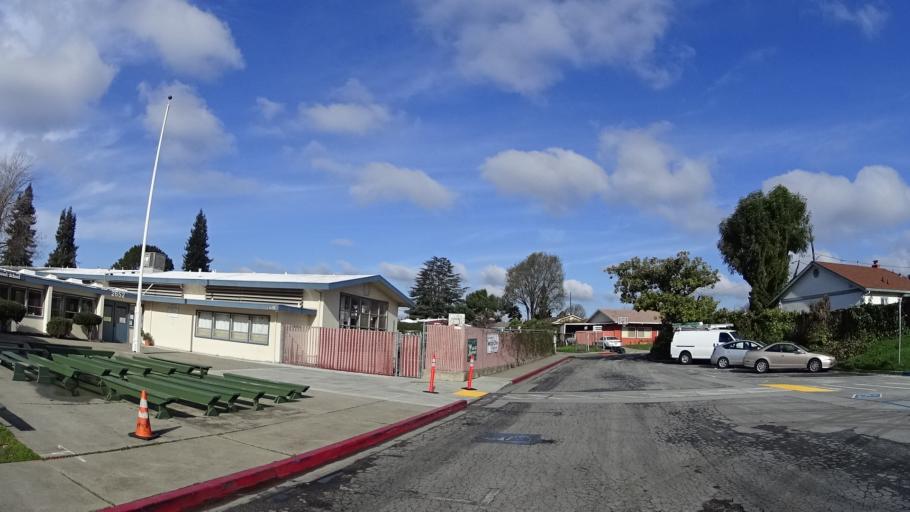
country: US
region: California
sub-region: Alameda County
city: Castro Valley
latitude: 37.6873
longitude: -122.0699
